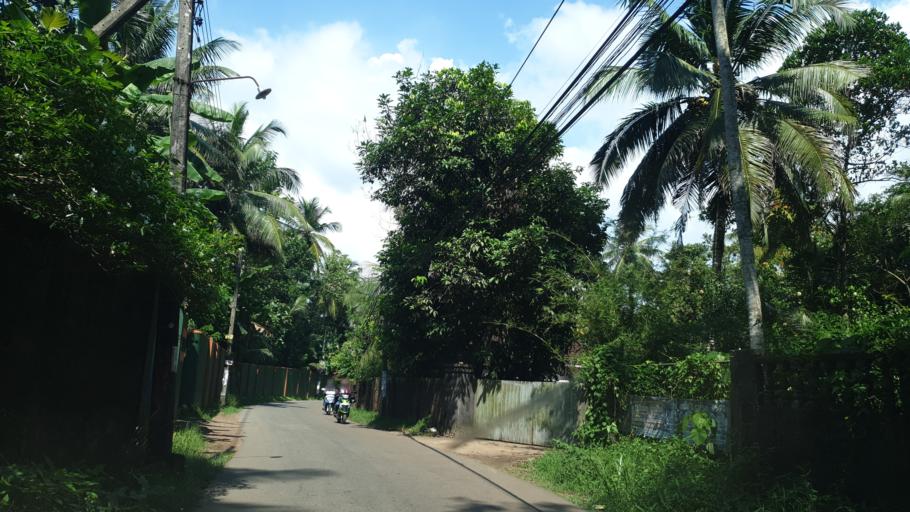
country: LK
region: Western
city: Panadura
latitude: 6.7076
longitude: 79.9581
